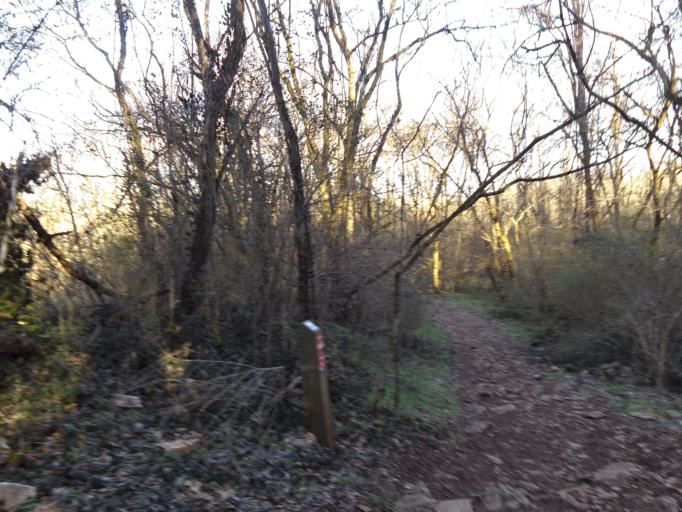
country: US
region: Tennessee
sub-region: Knox County
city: Knoxville
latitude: 35.9463
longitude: -83.8731
